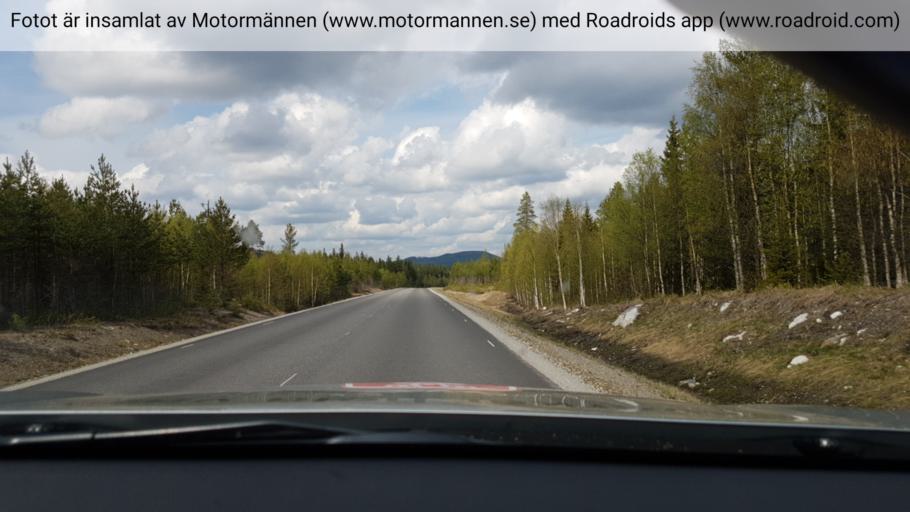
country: SE
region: Vaesterbotten
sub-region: Lycksele Kommun
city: Lycksele
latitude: 63.9961
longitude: 18.4710
